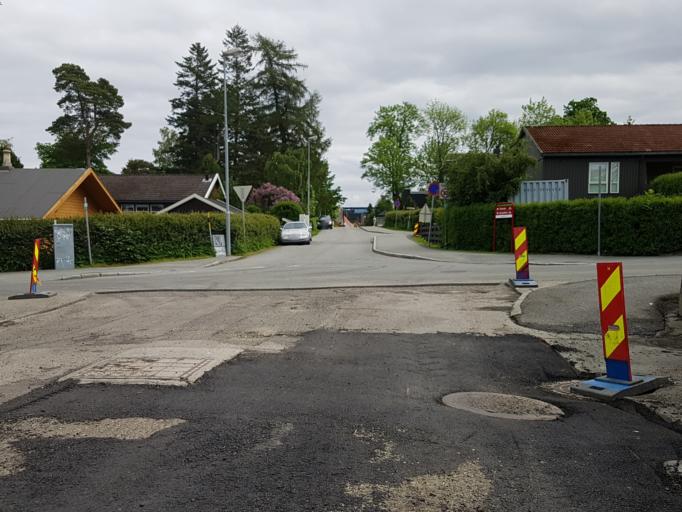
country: NO
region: Sor-Trondelag
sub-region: Trondheim
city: Trondheim
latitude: 63.4361
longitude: 10.4483
